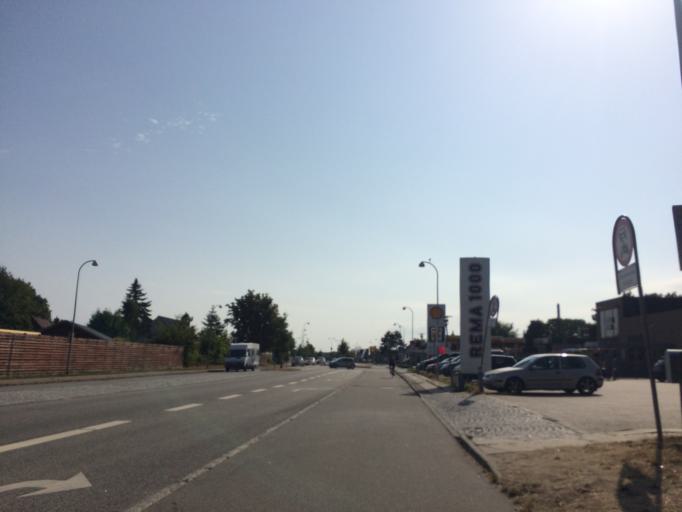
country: DK
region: Capital Region
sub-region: Ishoj Kommune
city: Ishoj
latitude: 55.6094
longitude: 12.3596
